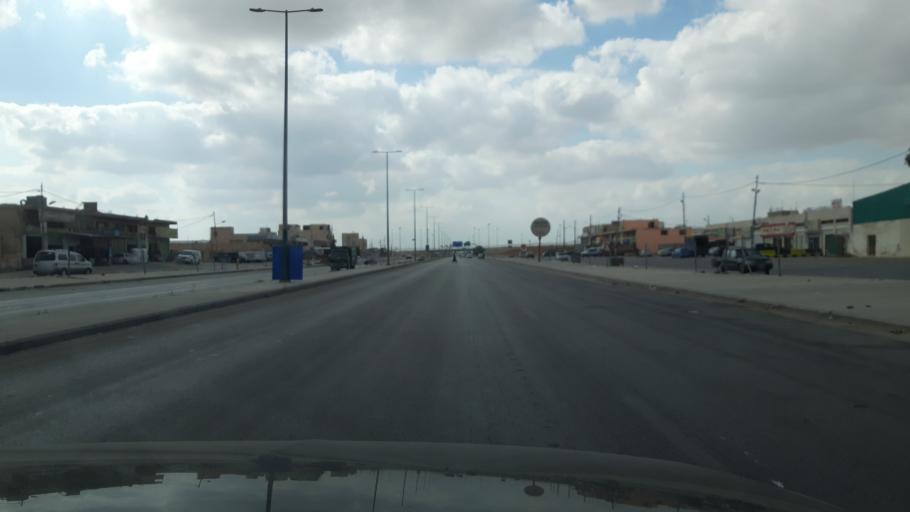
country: JO
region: Amman
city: Sahab
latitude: 31.8419
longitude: 36.0491
